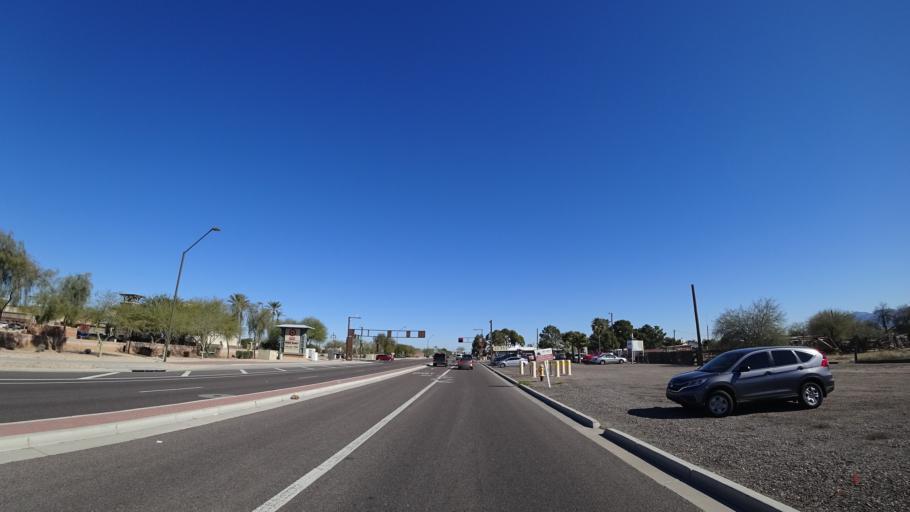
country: US
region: Arizona
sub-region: Maricopa County
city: Goodyear
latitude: 33.4356
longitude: -112.4229
